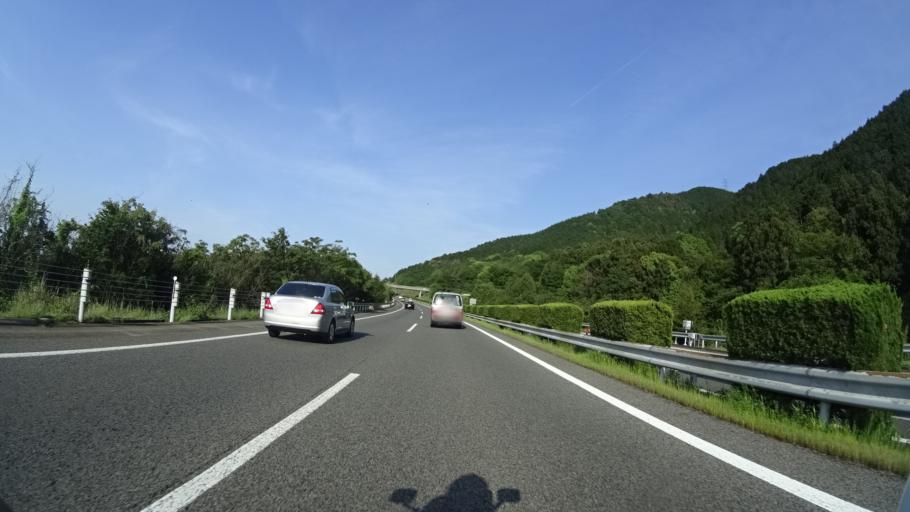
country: JP
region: Ehime
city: Niihama
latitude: 33.9505
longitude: 133.4338
